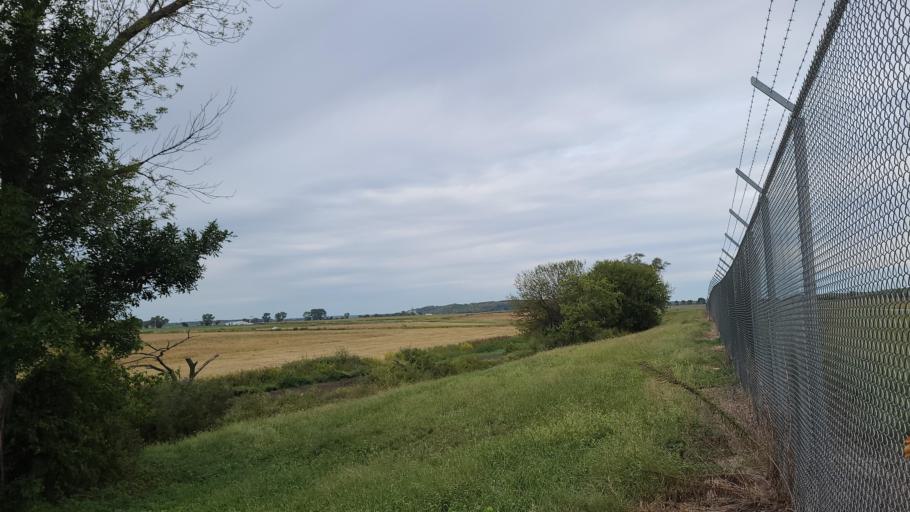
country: US
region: Kansas
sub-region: Douglas County
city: Lawrence
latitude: 39.0133
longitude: -95.2186
